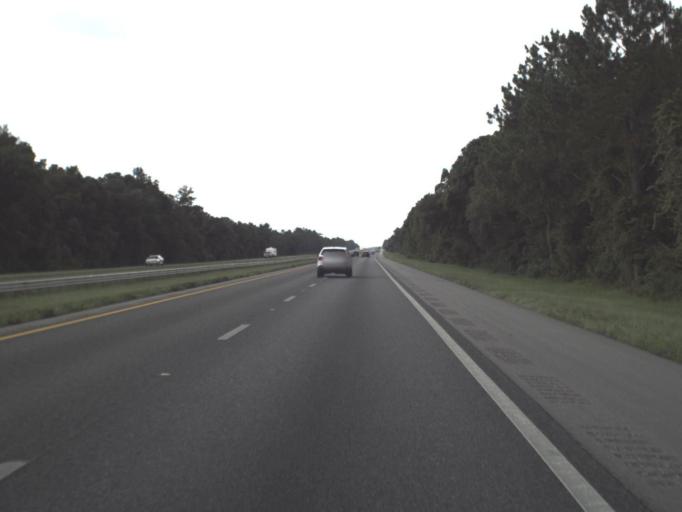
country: US
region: Florida
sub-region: Hernando County
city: Hill 'n Dale
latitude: 28.5551
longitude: -82.2371
